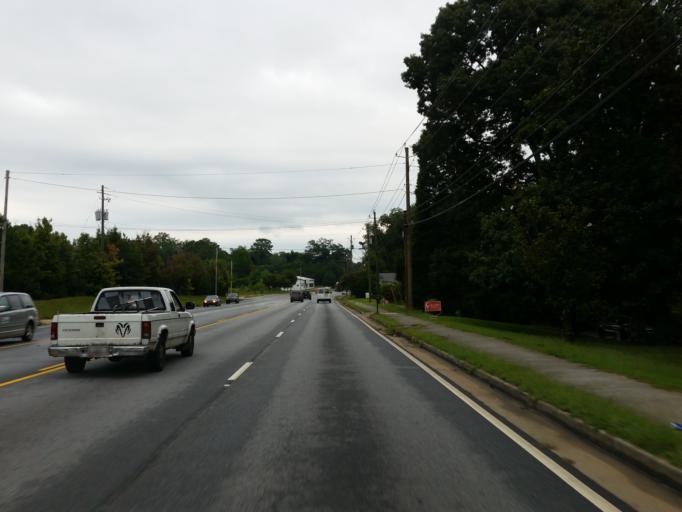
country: US
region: Georgia
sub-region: Cobb County
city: Mableton
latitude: 33.8128
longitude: -84.5490
